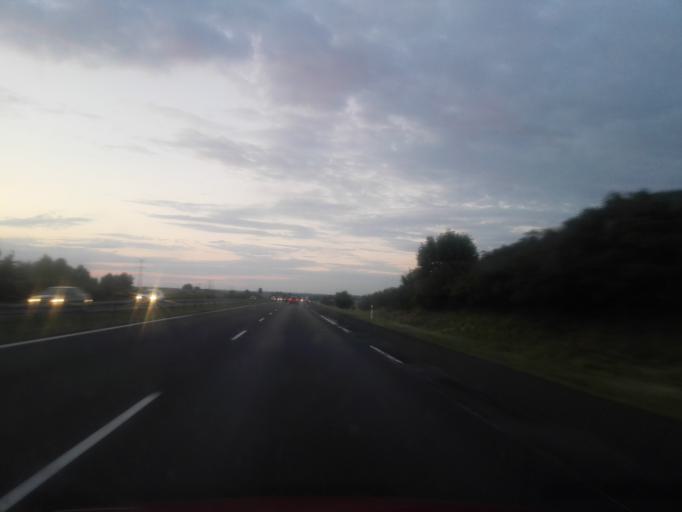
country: PL
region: Lodz Voivodeship
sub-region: Powiat radomszczanski
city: Kamiensk
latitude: 51.1960
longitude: 19.4749
